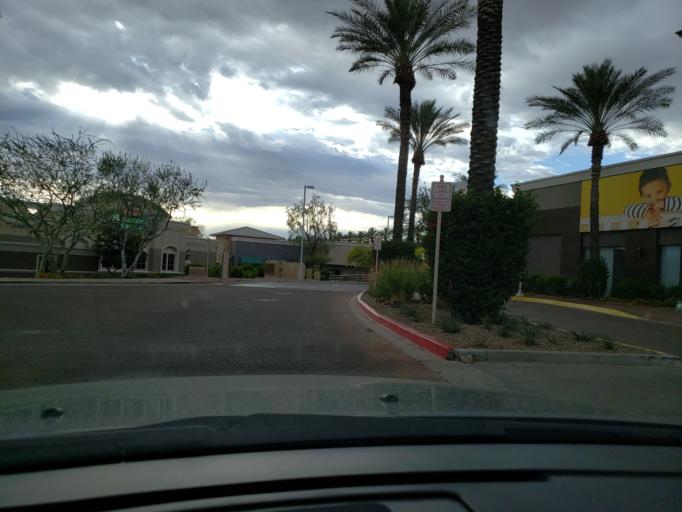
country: US
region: Arizona
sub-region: Maricopa County
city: Paradise Valley
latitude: 33.6760
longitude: -111.9740
